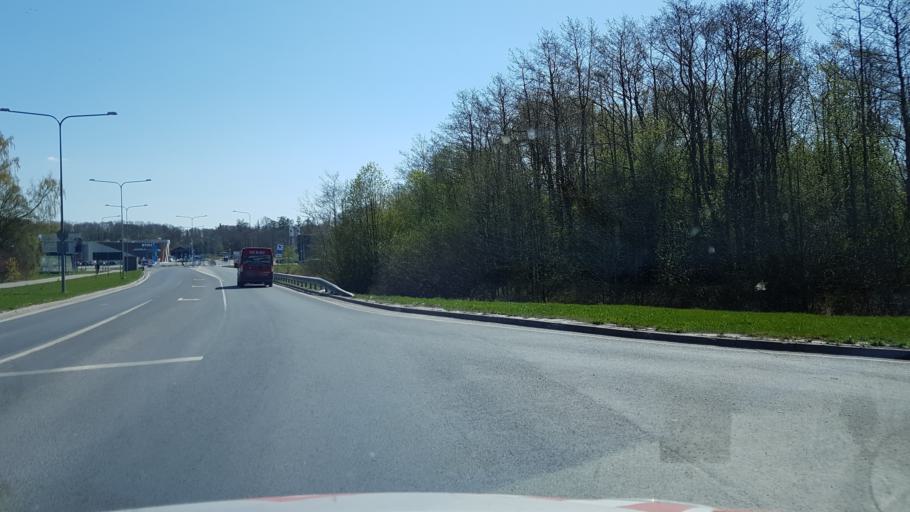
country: EE
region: Harju
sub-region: Viimsi vald
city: Haabneeme
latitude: 59.5071
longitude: 24.8224
